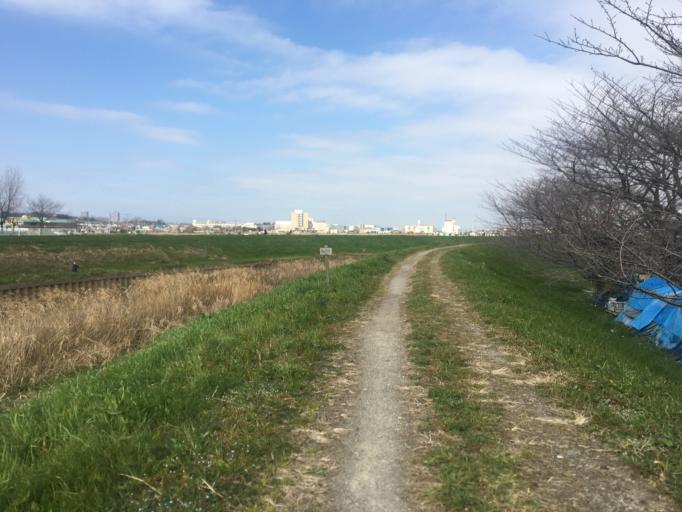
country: JP
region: Saitama
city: Shiki
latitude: 35.8507
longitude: 139.5615
